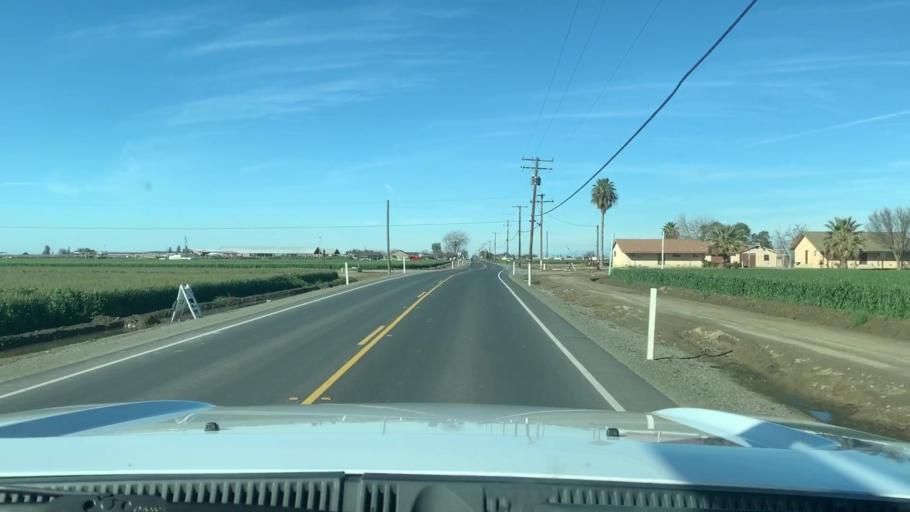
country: US
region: California
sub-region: Kings County
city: Corcoran
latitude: 36.1951
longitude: -119.4931
